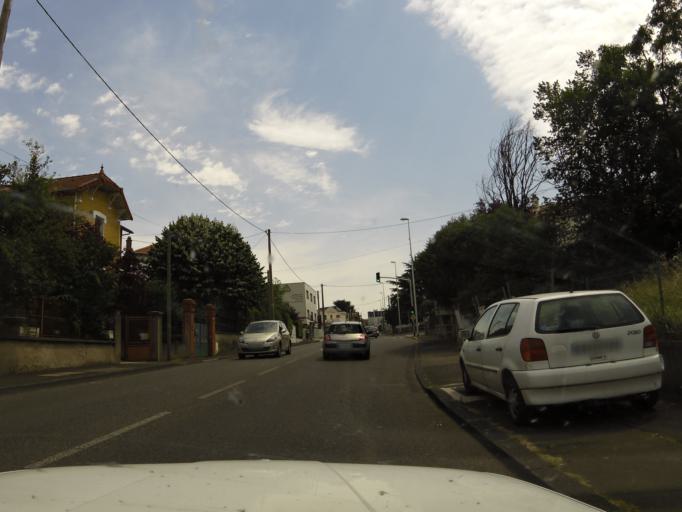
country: FR
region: Auvergne
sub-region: Departement du Puy-de-Dome
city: Beaumont
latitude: 45.7569
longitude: 3.0841
